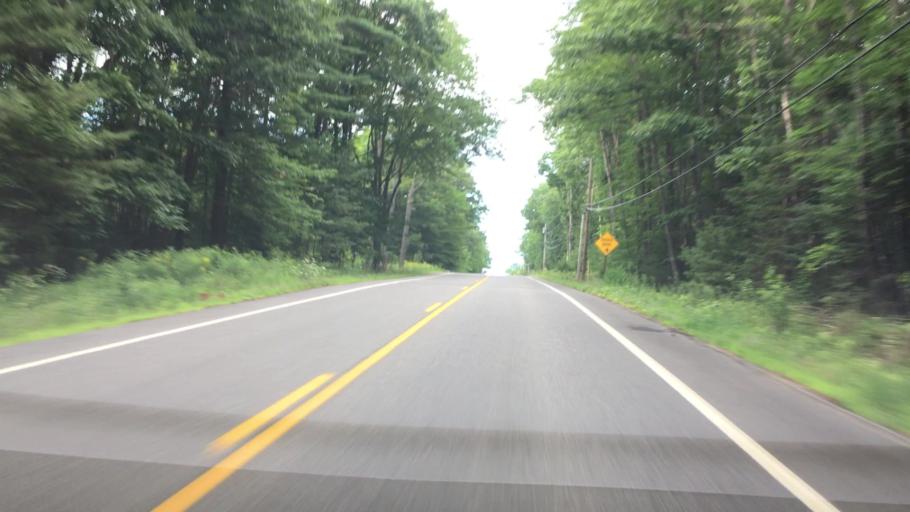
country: US
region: Maine
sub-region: Waldo County
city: Lincolnville
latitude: 44.3328
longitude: -69.0584
